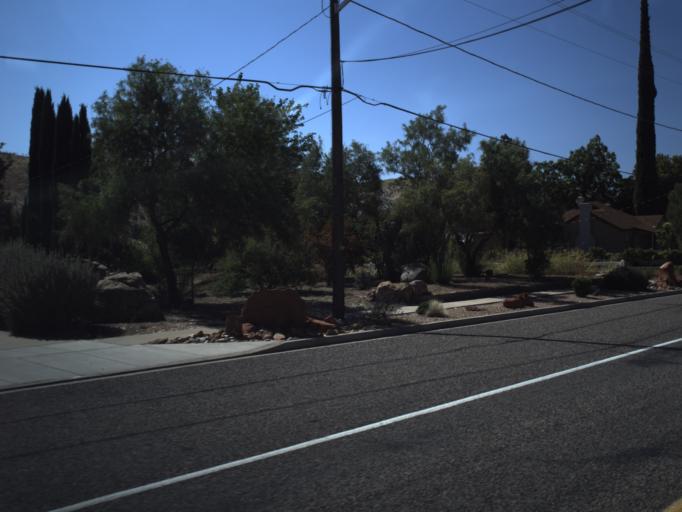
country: US
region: Utah
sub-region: Washington County
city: Toquerville
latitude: 37.2379
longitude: -113.3603
